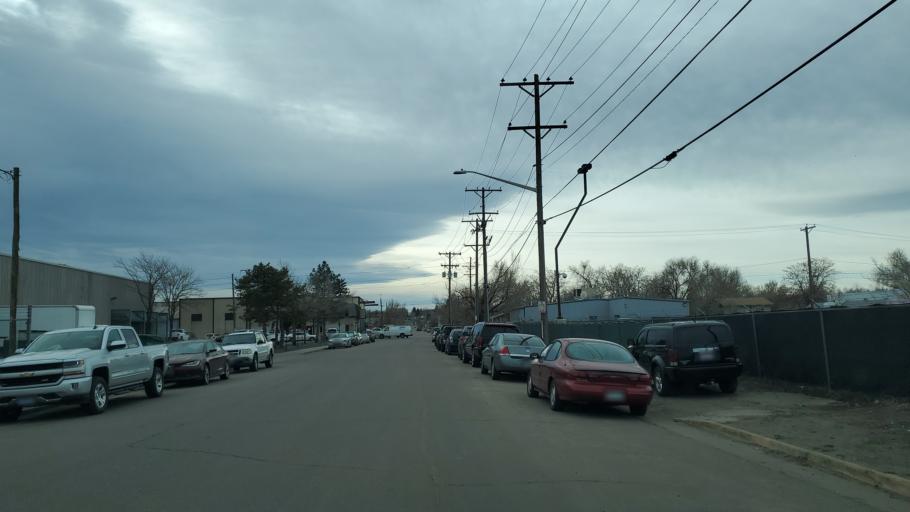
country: US
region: Colorado
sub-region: Denver County
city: Denver
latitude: 39.7159
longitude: -105.0086
